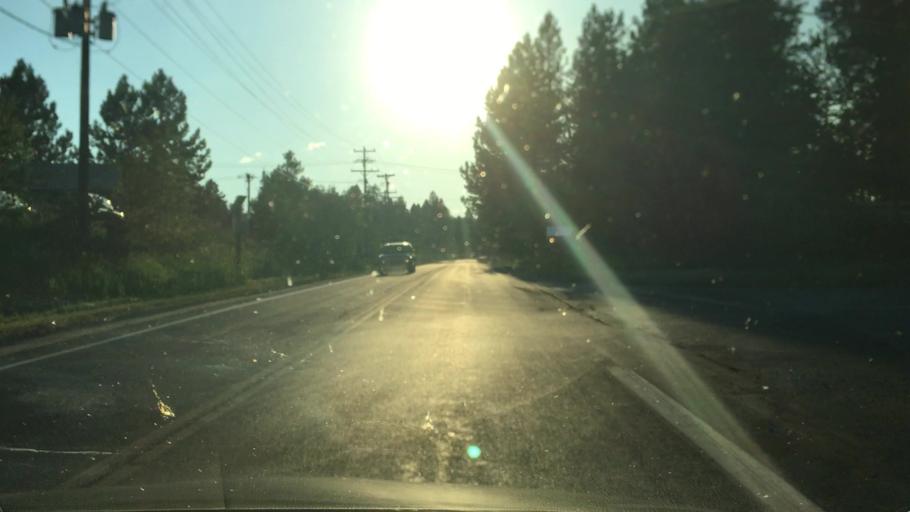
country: US
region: Idaho
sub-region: Valley County
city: McCall
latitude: 44.9127
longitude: -116.1226
